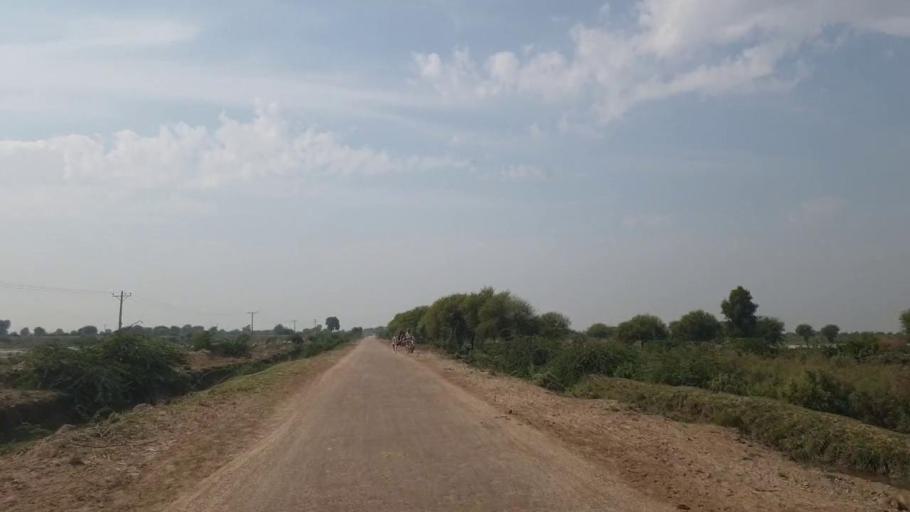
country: PK
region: Sindh
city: Rajo Khanani
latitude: 24.9686
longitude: 69.0137
